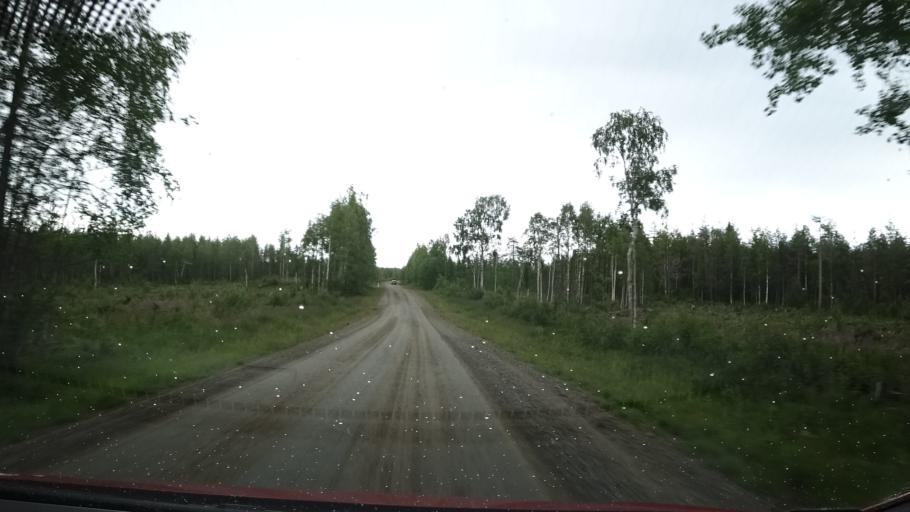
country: FI
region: Kainuu
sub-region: Kehys-Kainuu
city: Kuhmo
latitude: 63.9453
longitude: 29.2148
